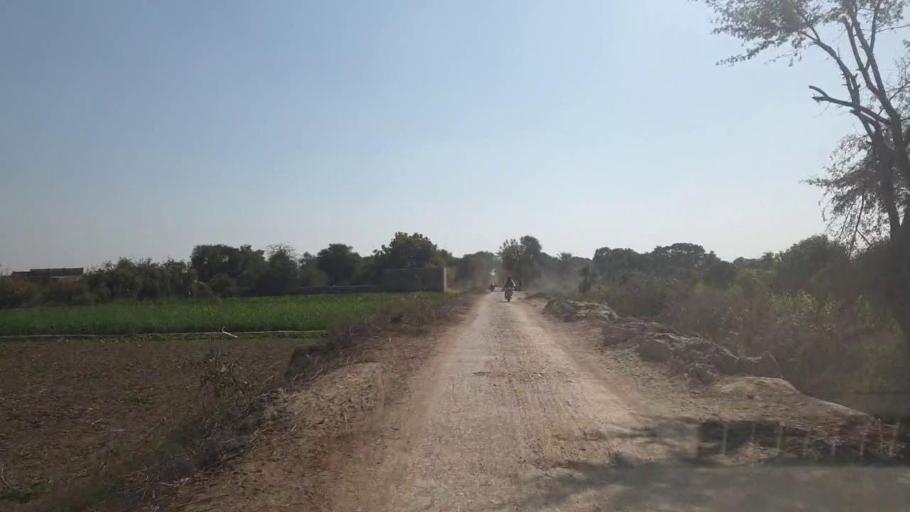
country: PK
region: Sindh
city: Chambar
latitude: 25.3118
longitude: 68.7408
